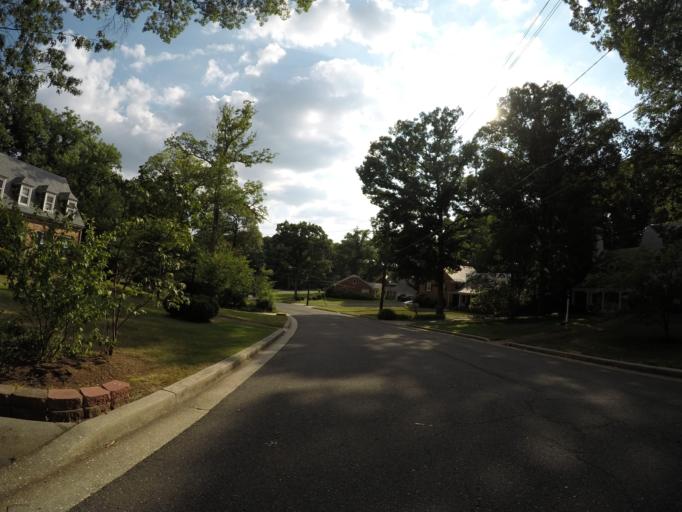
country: US
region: Maryland
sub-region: Prince George's County
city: University Park
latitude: 38.9790
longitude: -76.9507
